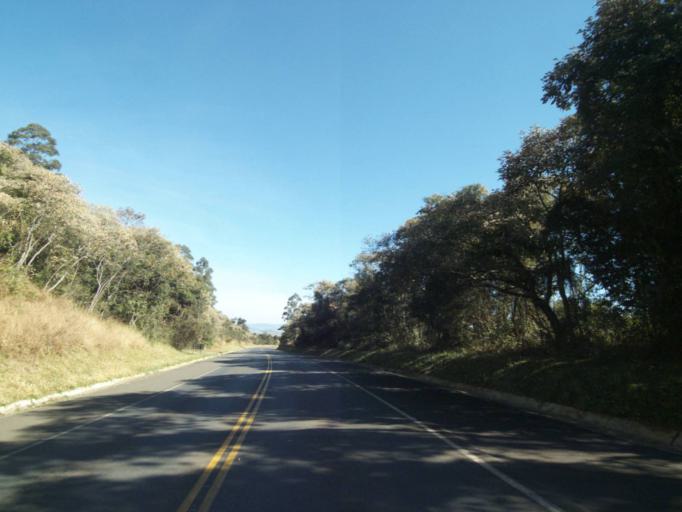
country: BR
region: Parana
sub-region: Tibagi
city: Tibagi
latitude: -24.4085
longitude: -50.3530
